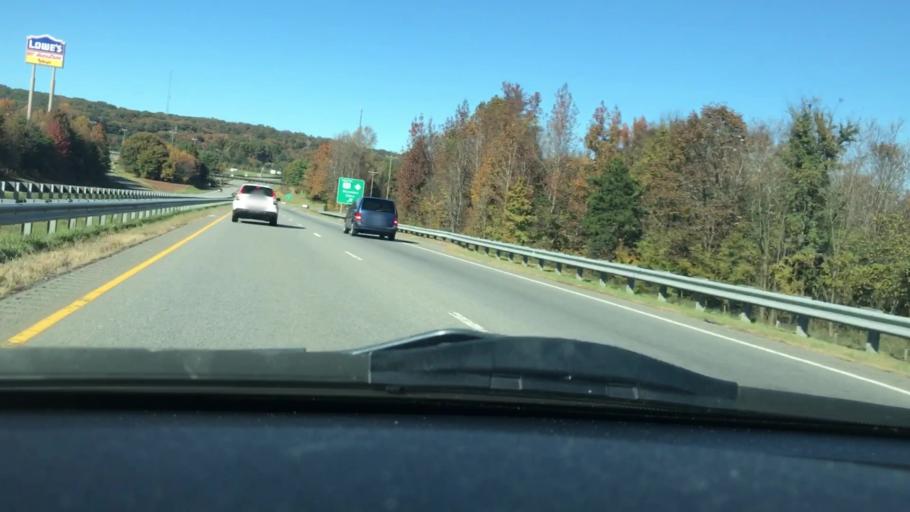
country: US
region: North Carolina
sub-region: Rockingham County
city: Mayodan
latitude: 36.4114
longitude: -79.9377
